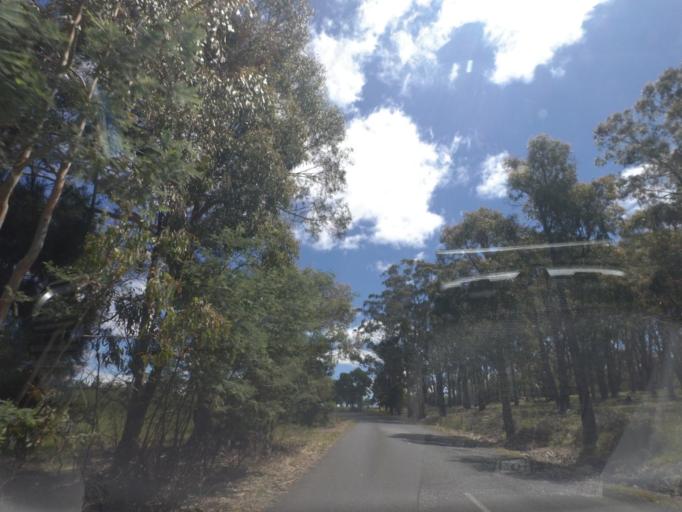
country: AU
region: Victoria
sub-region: Mount Alexander
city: Castlemaine
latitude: -37.3173
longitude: 144.1799
